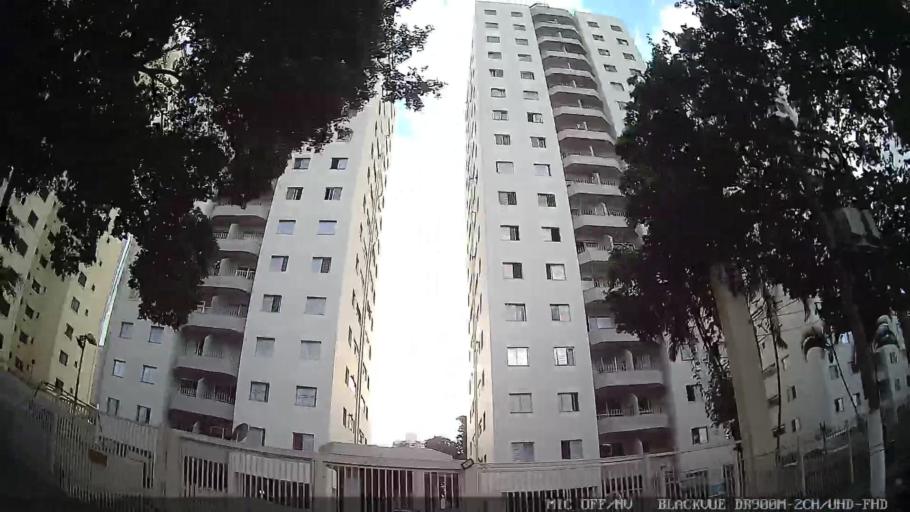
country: BR
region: Sao Paulo
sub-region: Sao Paulo
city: Sao Paulo
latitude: -23.5411
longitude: -46.5700
